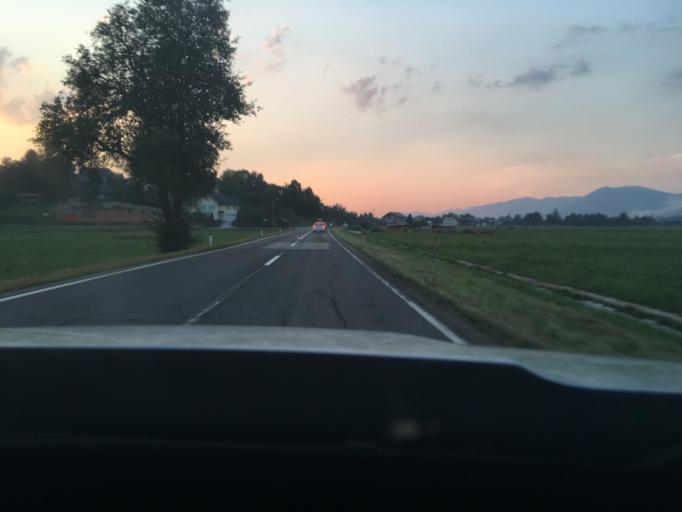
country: SI
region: Ribnica
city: Ribnica
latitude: 45.7016
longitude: 14.7593
